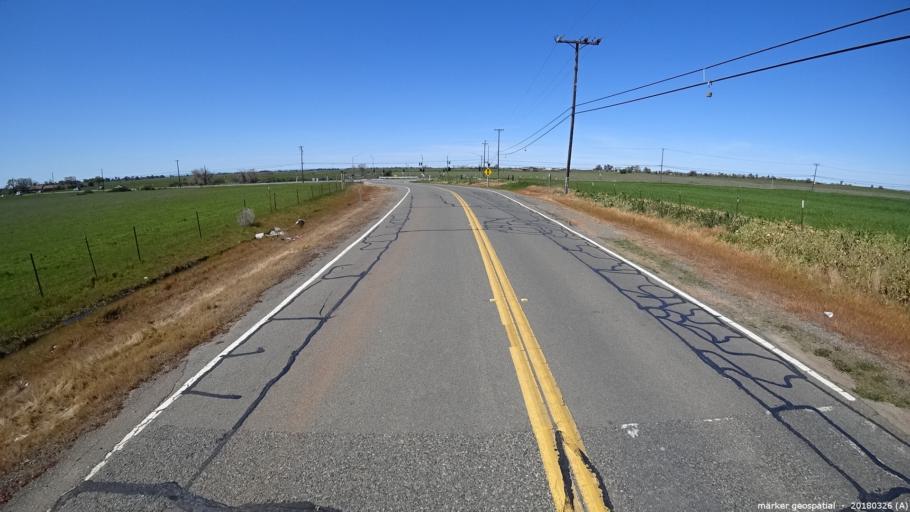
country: US
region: California
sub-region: Sacramento County
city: Wilton
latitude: 38.4716
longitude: -121.2553
